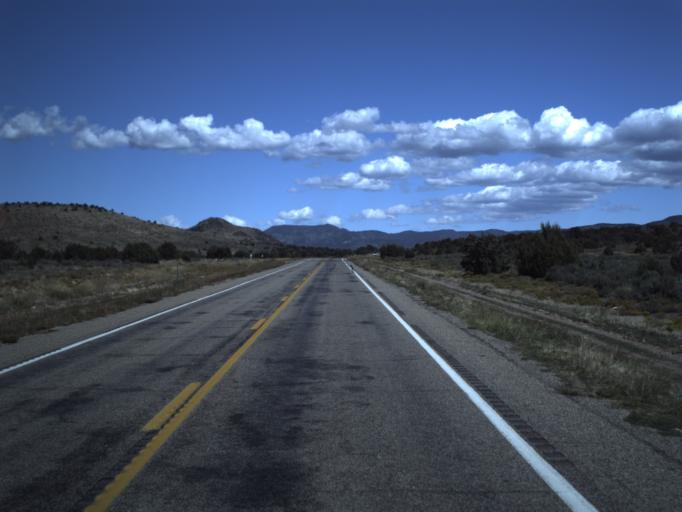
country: US
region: Utah
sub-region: Washington County
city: Ivins
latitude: 37.3546
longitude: -113.6823
